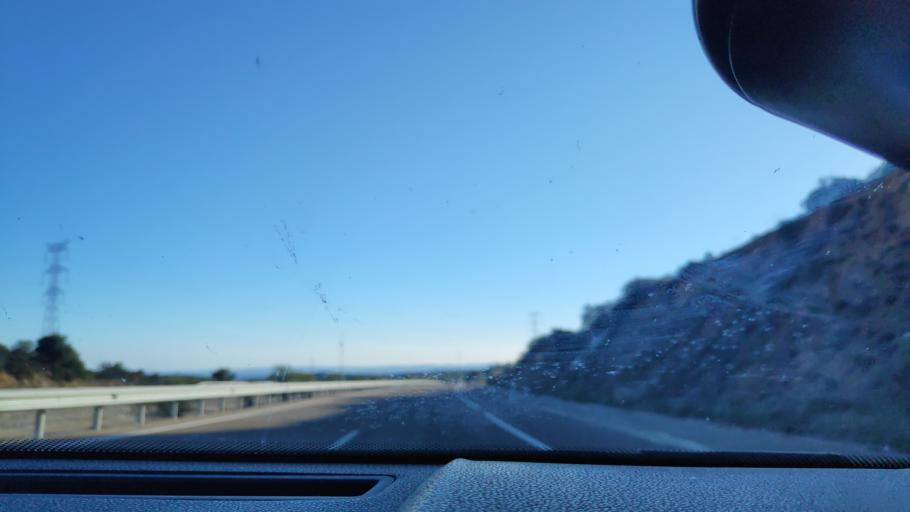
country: ES
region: Andalusia
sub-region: Provincia de Sevilla
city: Gerena
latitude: 37.5964
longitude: -6.1239
